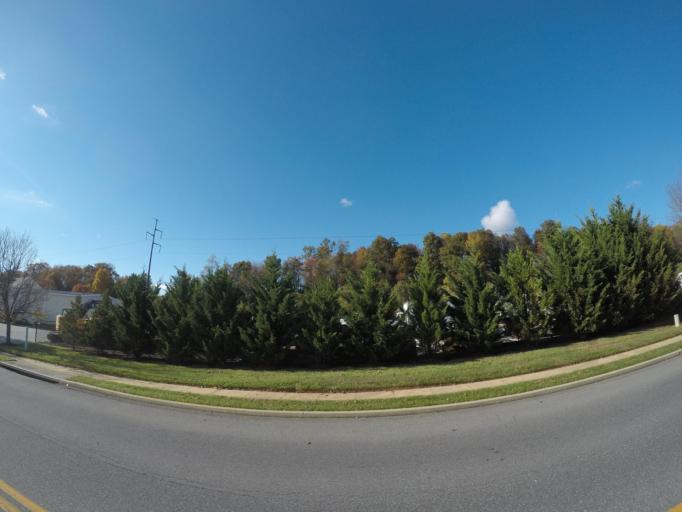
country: US
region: Maryland
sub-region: Carroll County
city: Mount Airy
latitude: 39.3696
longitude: -77.1721
